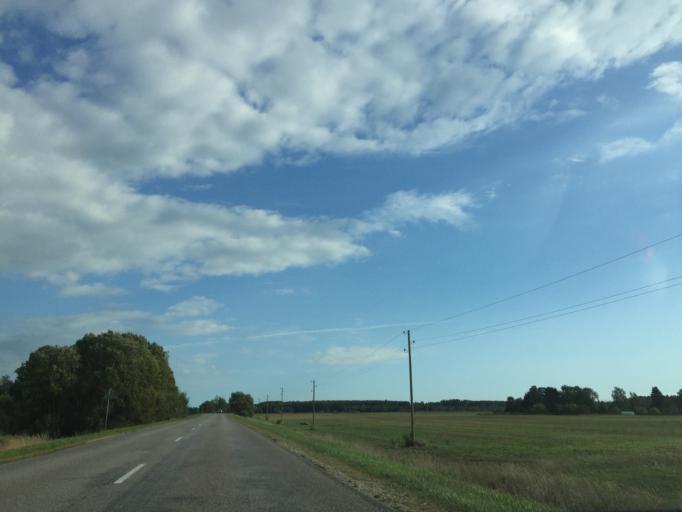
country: LV
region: Limbazu Rajons
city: Limbazi
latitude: 57.5063
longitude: 24.5024
